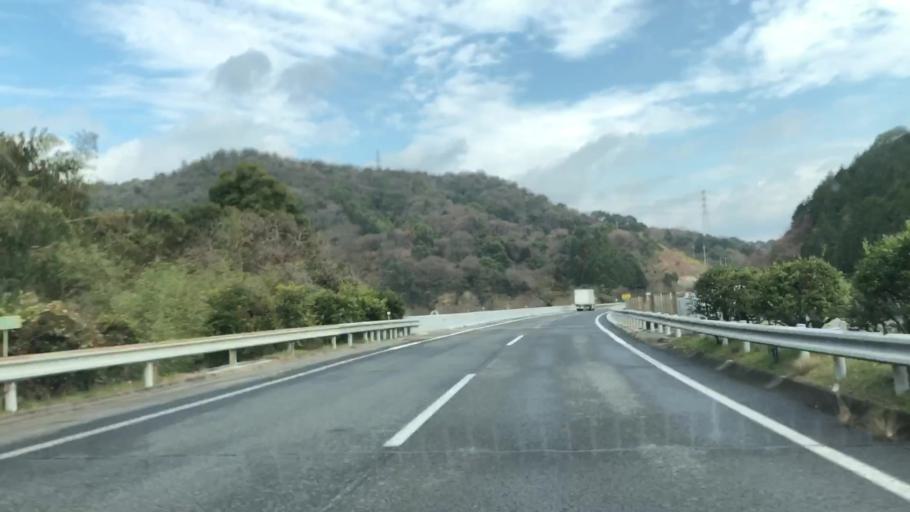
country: JP
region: Saga Prefecture
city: Kanzakimachi-kanzaki
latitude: 33.3373
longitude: 130.3301
